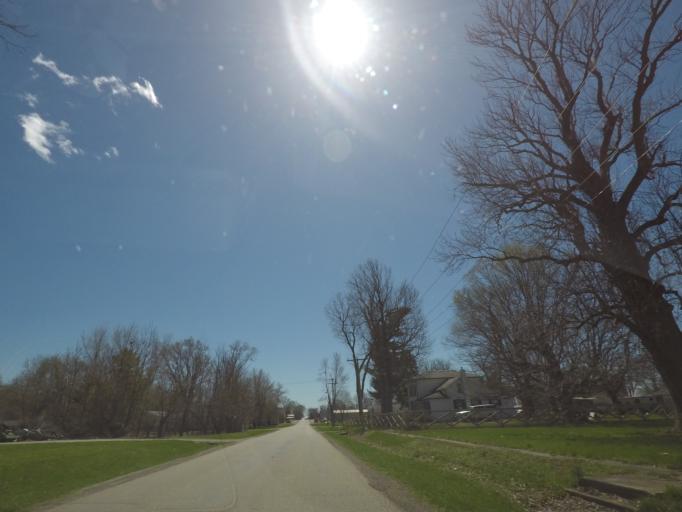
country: US
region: Illinois
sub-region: Logan County
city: Atlanta
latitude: 40.1463
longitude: -89.1933
